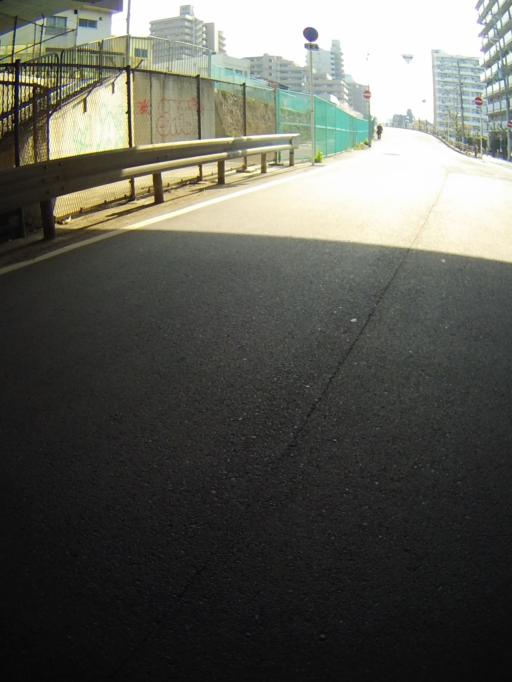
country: JP
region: Hyogo
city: Amagasaki
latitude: 34.6864
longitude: 135.4520
